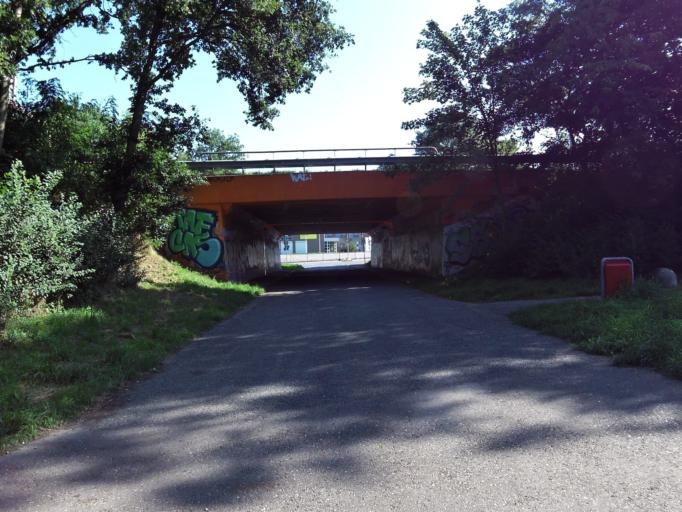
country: NL
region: Limburg
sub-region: Gemeente Heerlen
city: Heerlen
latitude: 50.8875
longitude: 5.9639
